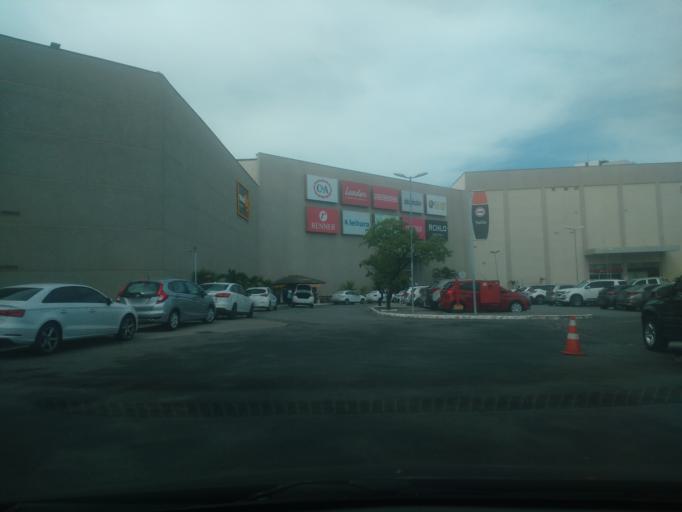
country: BR
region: Alagoas
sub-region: Maceio
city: Maceio
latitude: -9.6485
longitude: -35.7148
